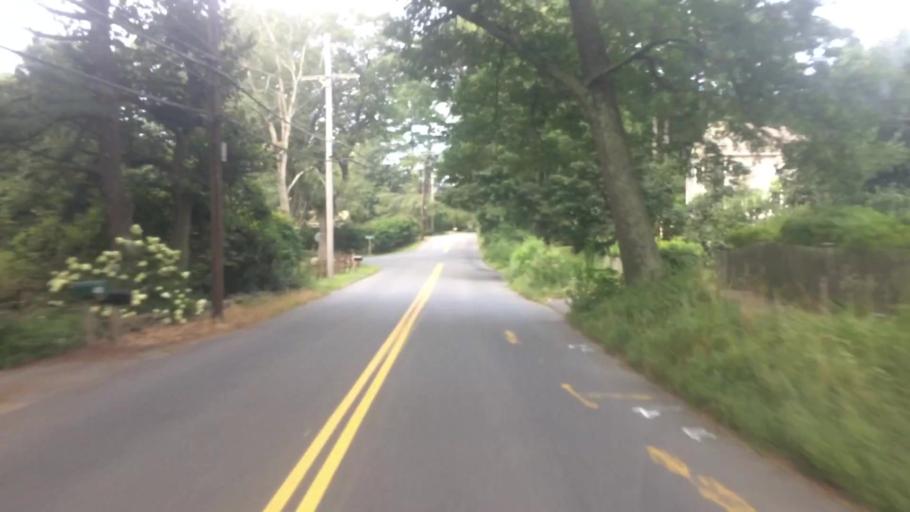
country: US
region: Massachusetts
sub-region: Middlesex County
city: Acton
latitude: 42.4645
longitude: -71.4265
